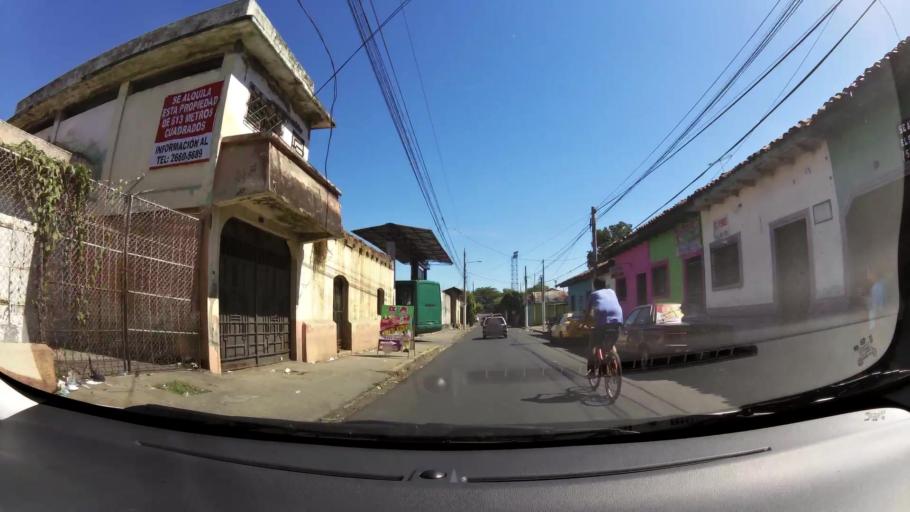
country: SV
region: San Miguel
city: San Miguel
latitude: 13.4834
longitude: -88.1712
